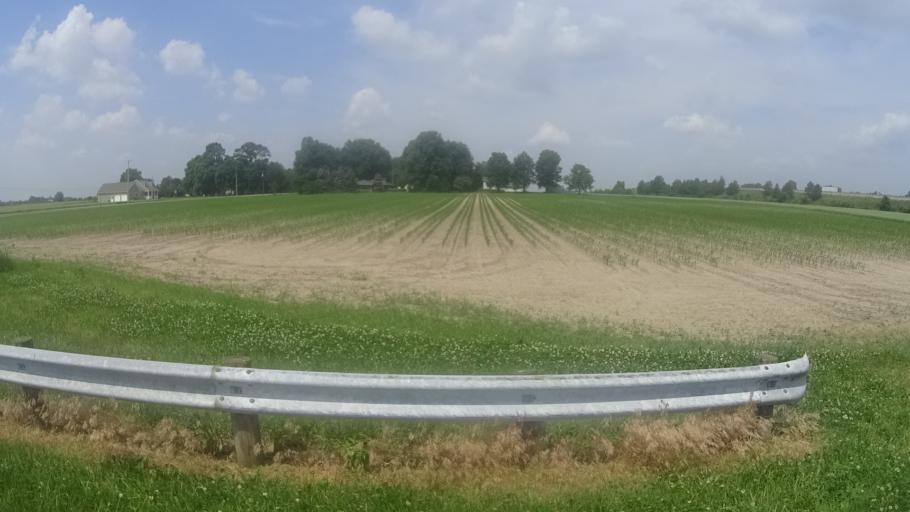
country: US
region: Ohio
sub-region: Huron County
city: Monroeville
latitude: 41.3343
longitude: -82.6936
